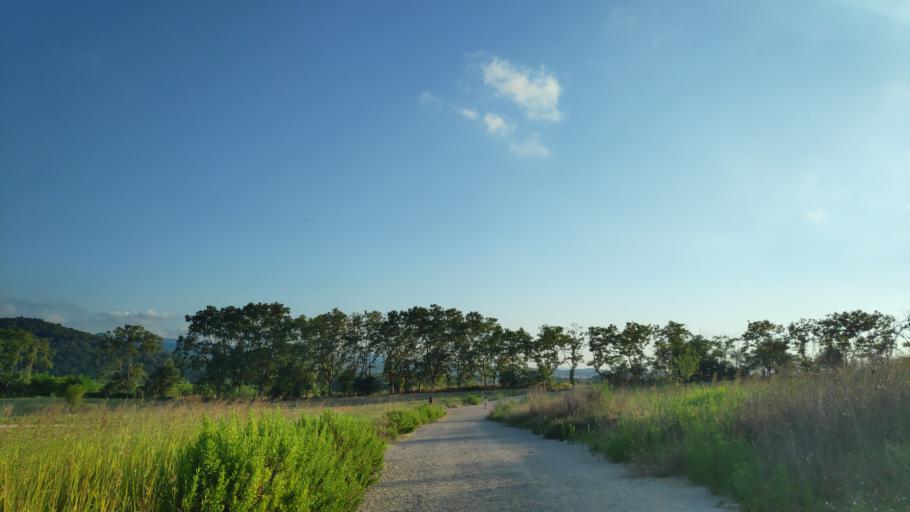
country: ES
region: Catalonia
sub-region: Provincia de Barcelona
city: Cerdanyola del Valles
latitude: 41.4899
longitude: 2.1172
